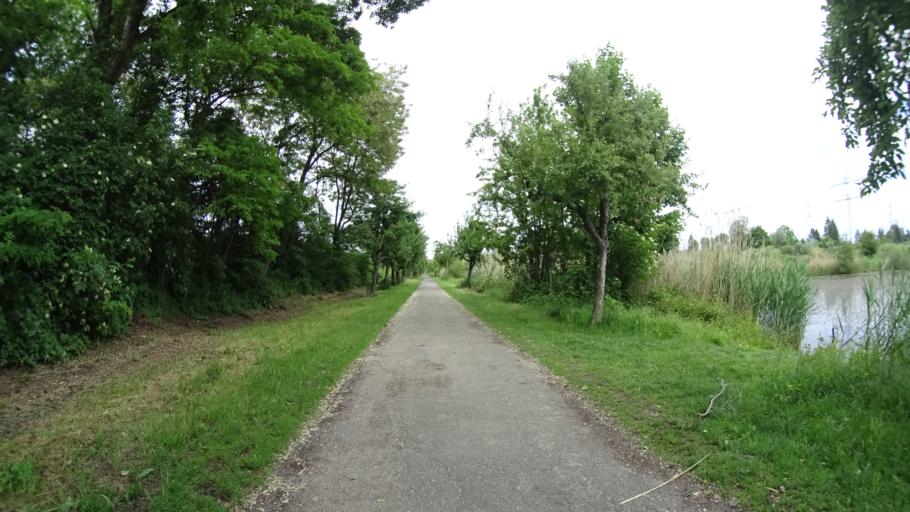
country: DE
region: Baden-Wuerttemberg
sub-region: Karlsruhe Region
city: Rheinstetten
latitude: 49.0008
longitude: 8.3157
